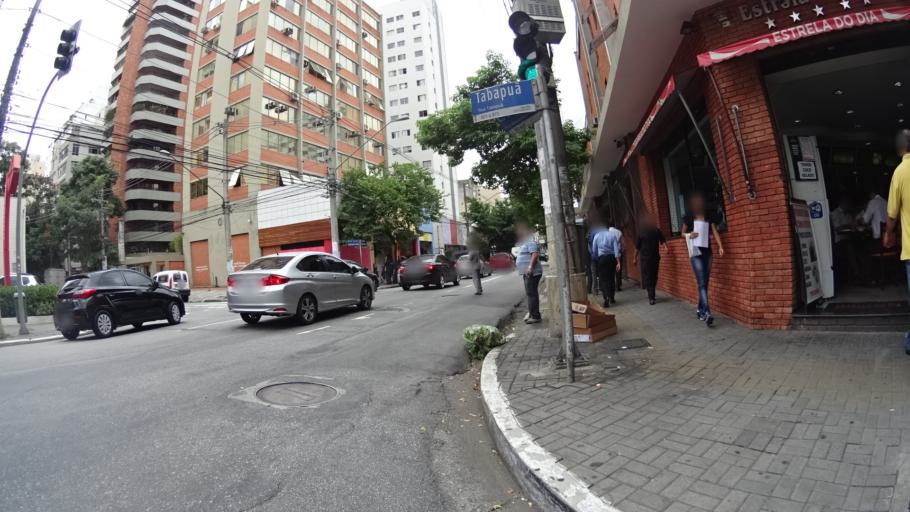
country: BR
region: Sao Paulo
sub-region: Sao Paulo
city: Sao Paulo
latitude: -23.5844
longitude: -46.6801
